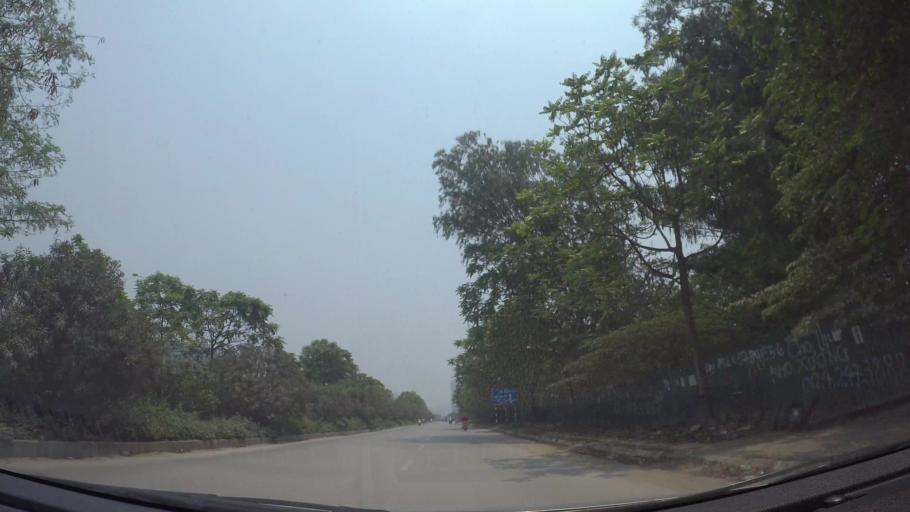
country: VN
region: Ha Noi
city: Thanh Xuan
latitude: 21.0042
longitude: 105.7707
